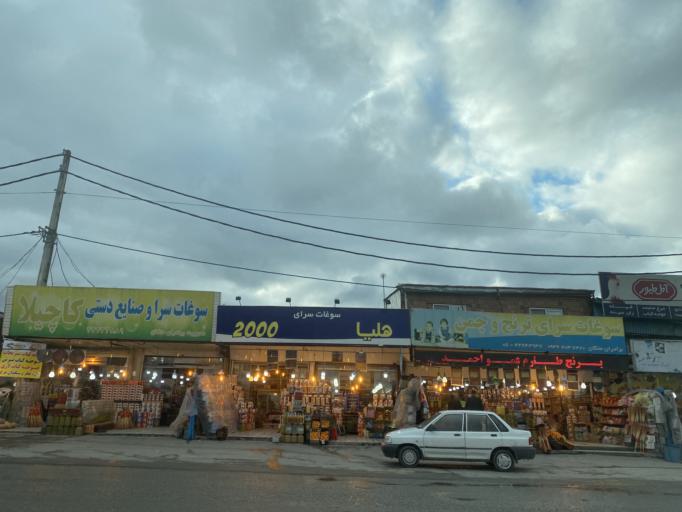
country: IR
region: Mazandaran
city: Amol
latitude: 36.4301
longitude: 52.3487
